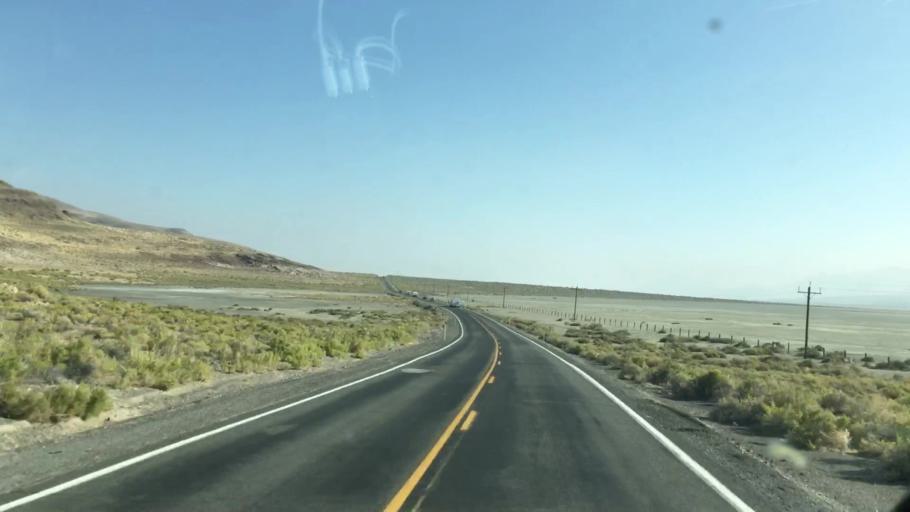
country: US
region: Nevada
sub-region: Lyon County
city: Fernley
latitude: 40.0714
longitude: -119.3746
